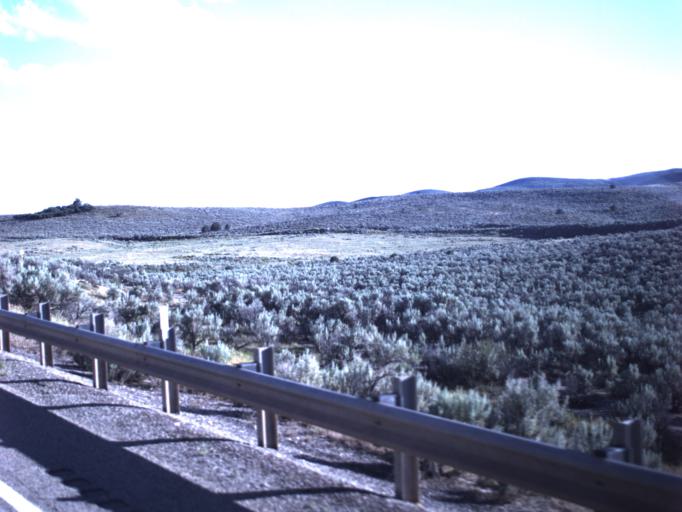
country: US
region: Utah
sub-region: Sanpete County
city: Fairview
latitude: 39.7242
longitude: -111.4733
